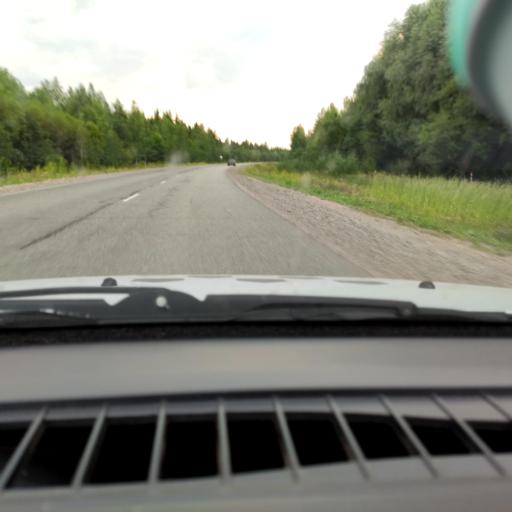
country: RU
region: Udmurtiya
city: Debesy
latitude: 57.6039
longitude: 53.4603
